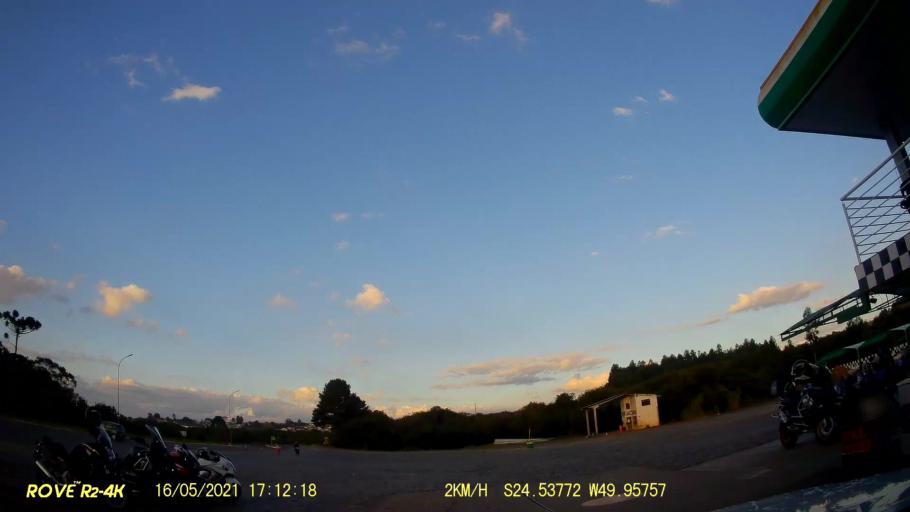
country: BR
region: Parana
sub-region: Pirai Do Sul
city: Pirai do Sul
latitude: -24.5378
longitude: -49.9577
